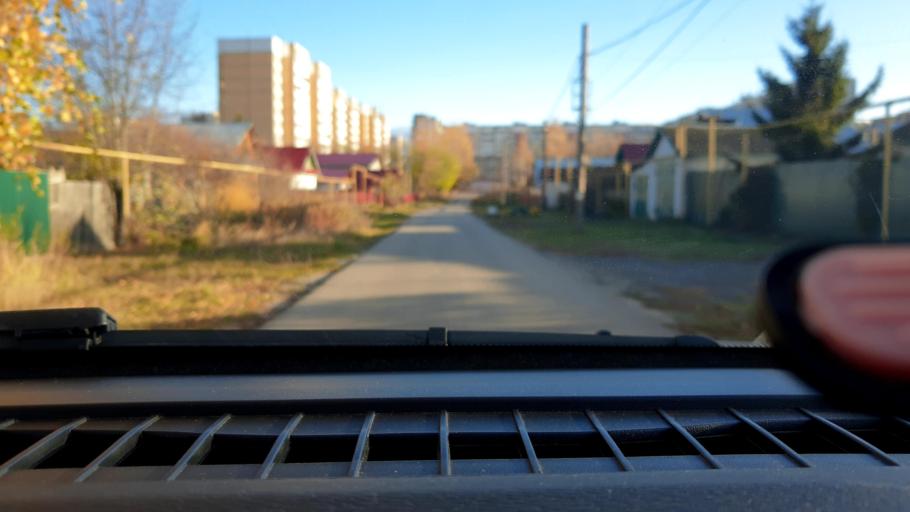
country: RU
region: Nizjnij Novgorod
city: Gorbatovka
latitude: 56.3707
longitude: 43.8049
